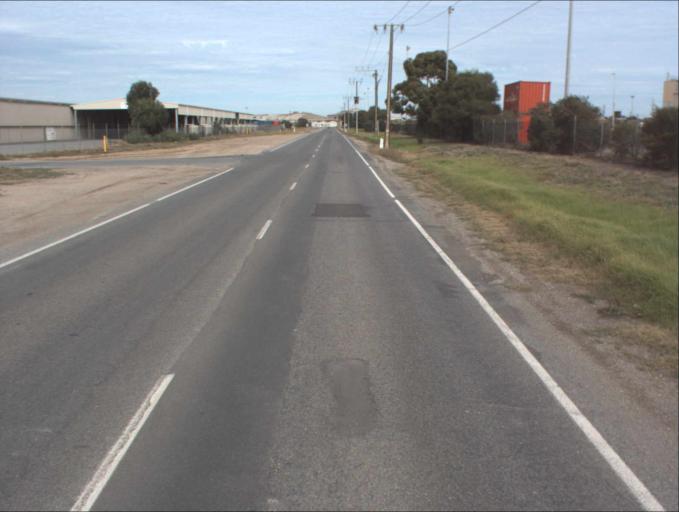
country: AU
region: South Australia
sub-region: Port Adelaide Enfield
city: Birkenhead
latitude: -34.8270
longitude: 138.5196
